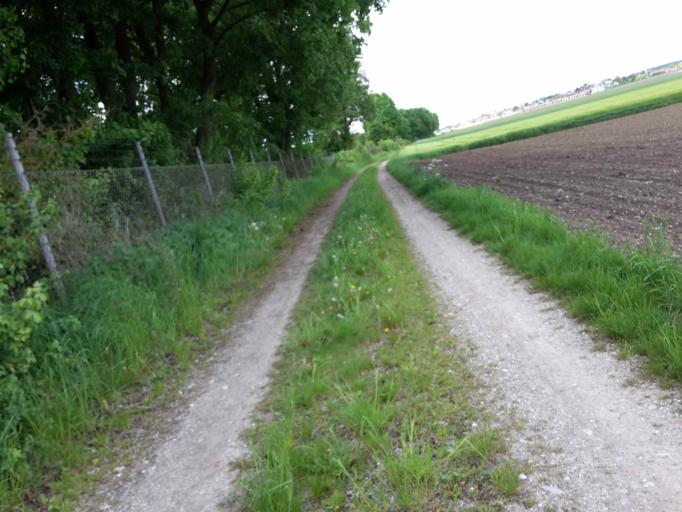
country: DE
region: Bavaria
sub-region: Upper Bavaria
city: Maisach
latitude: 48.2107
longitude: 11.2788
